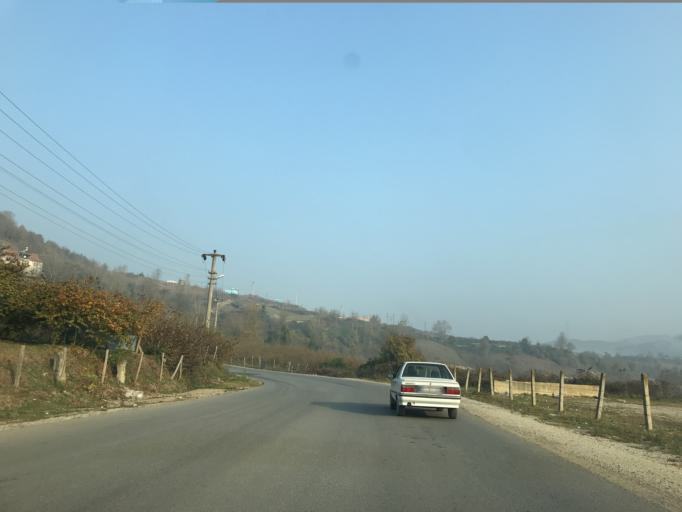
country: TR
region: Duzce
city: Cumayeri
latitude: 40.8872
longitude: 30.9522
